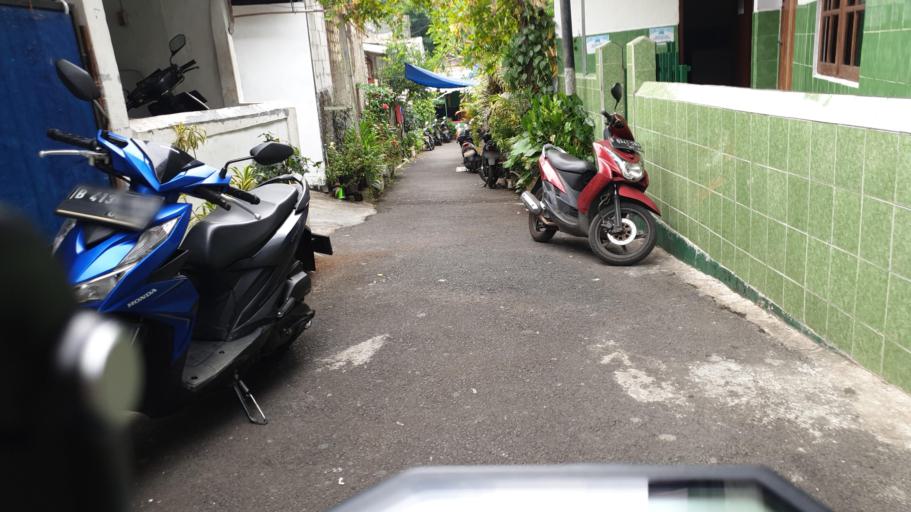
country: ID
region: Jakarta Raya
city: Jakarta
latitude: -6.2710
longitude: 106.7932
